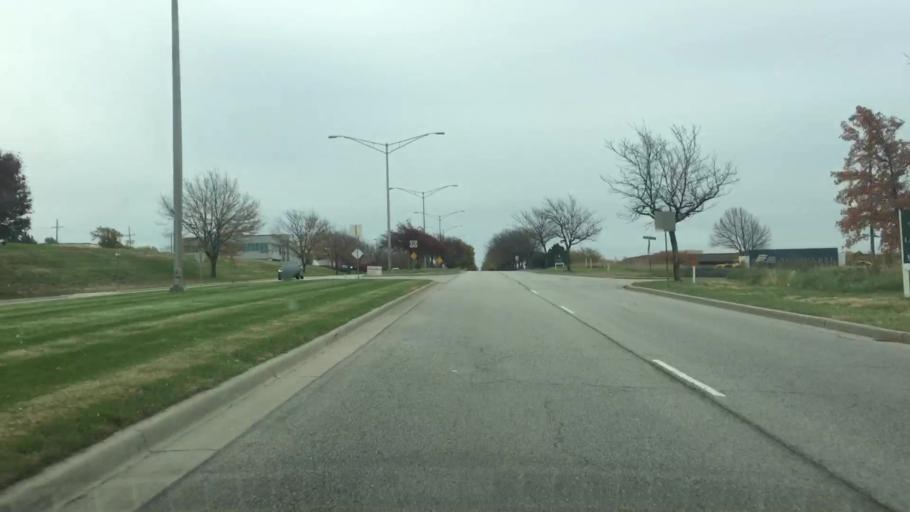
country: US
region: Kansas
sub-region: Johnson County
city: Lenexa
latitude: 38.9273
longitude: -94.7749
